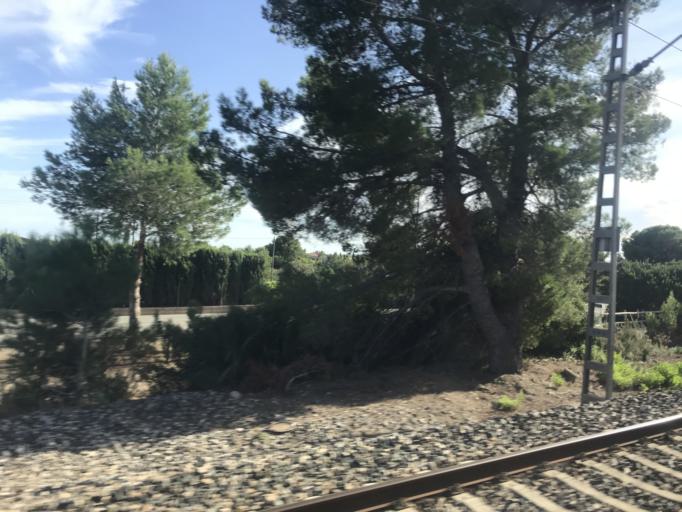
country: ES
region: Catalonia
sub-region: Provincia de Tarragona
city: Camarles
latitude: 40.7656
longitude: 0.6559
